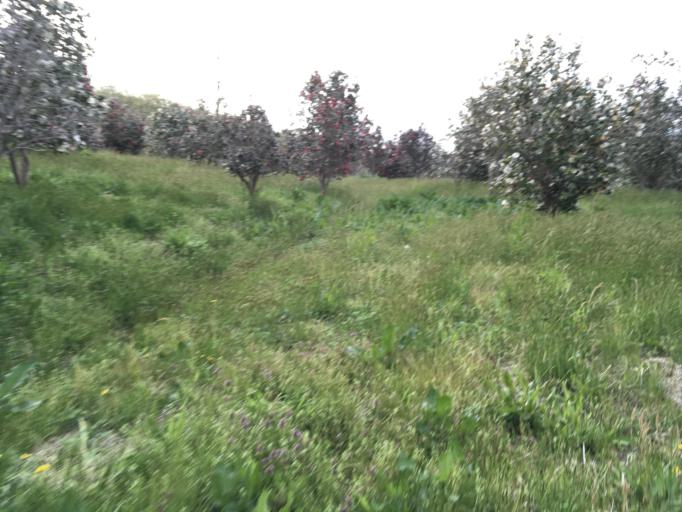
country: JP
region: Iwate
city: Ichinoseki
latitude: 38.8440
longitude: 141.3213
